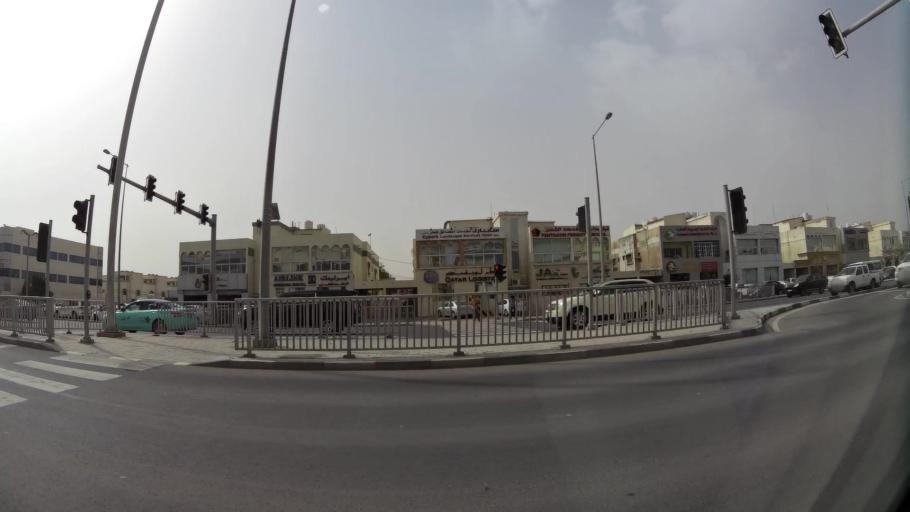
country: QA
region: Baladiyat ad Dawhah
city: Doha
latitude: 25.2630
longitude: 51.5318
